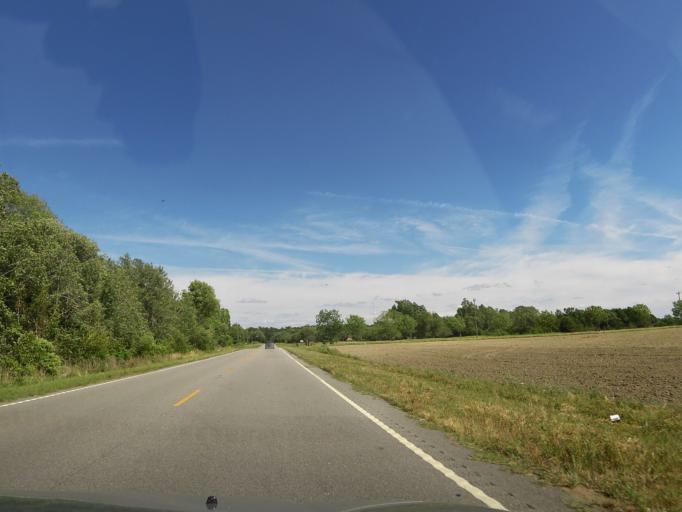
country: US
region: South Carolina
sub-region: Barnwell County
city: Blackville
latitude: 33.3684
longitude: -81.3340
